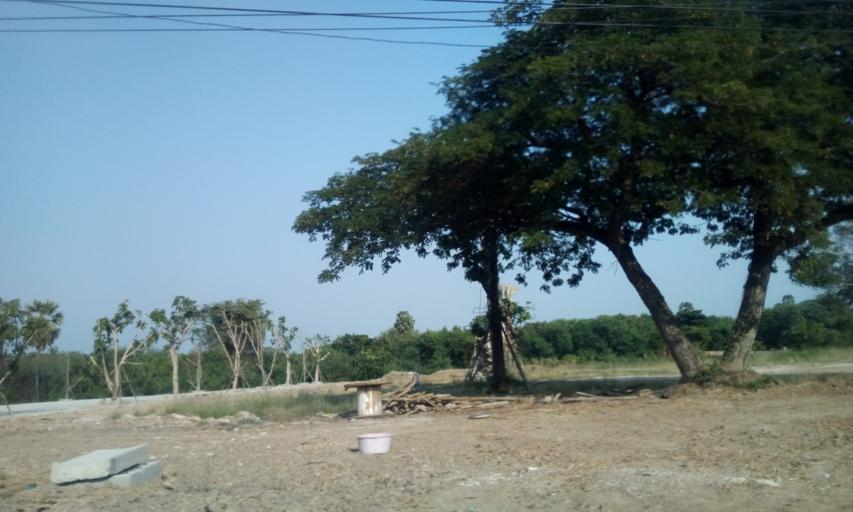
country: TH
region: Sing Buri
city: Sing Buri
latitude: 14.8500
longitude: 100.3907
